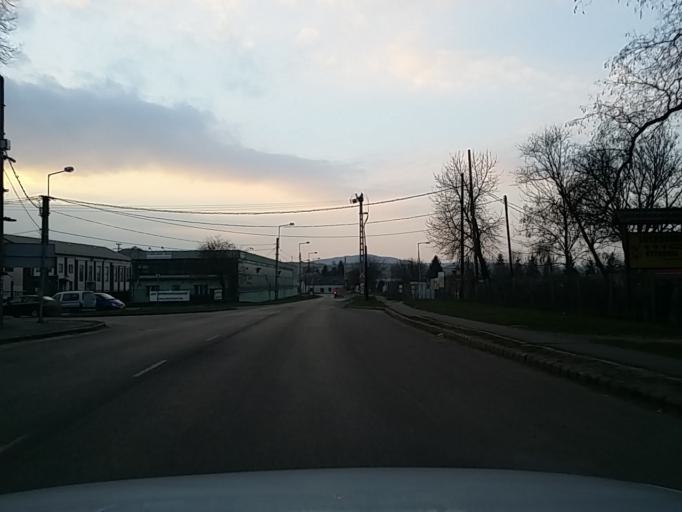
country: HU
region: Nograd
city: Batonyterenye
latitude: 47.9774
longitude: 19.8201
